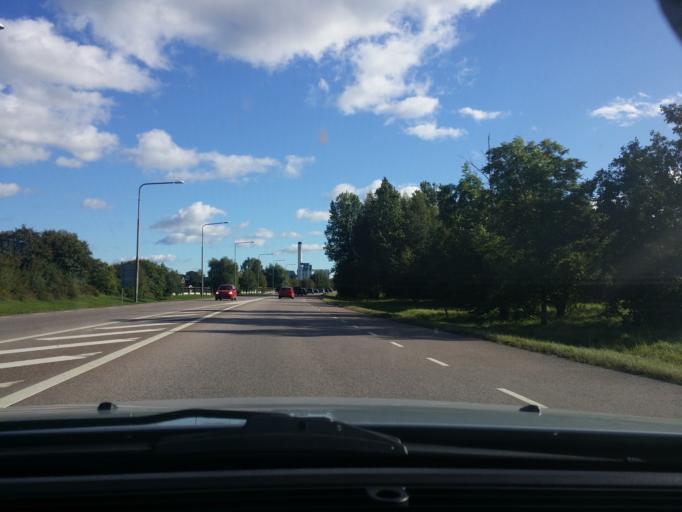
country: SE
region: Vaestmanland
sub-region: Vasteras
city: Vasteras
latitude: 59.6017
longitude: 16.4932
